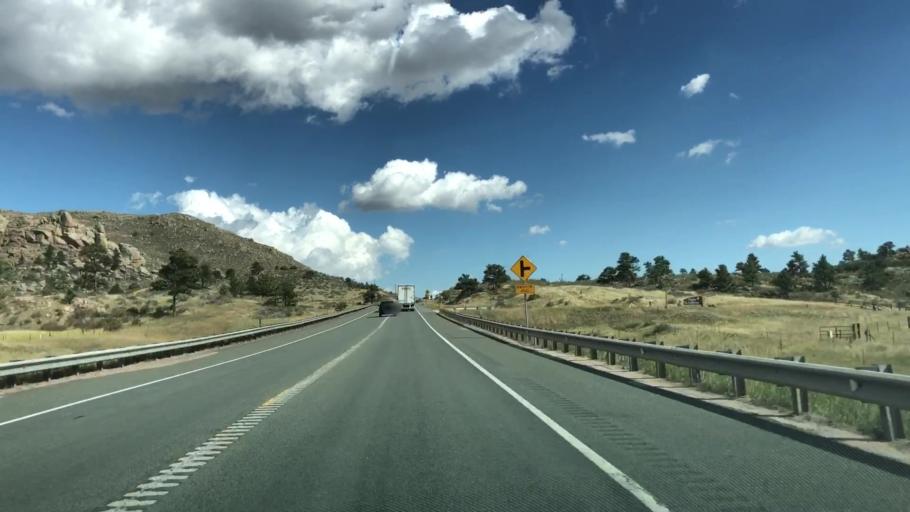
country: US
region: Colorado
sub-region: Larimer County
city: Laporte
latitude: 40.9590
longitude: -105.3594
